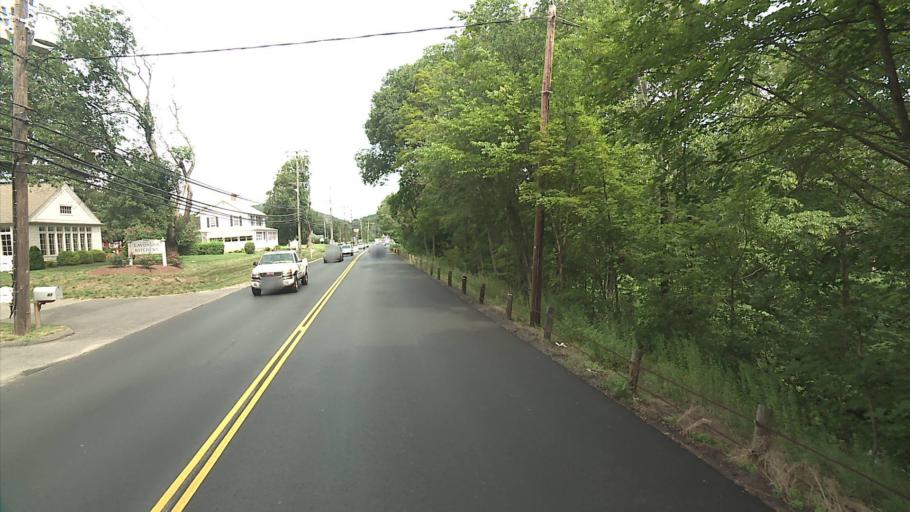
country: US
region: Connecticut
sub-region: New Haven County
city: Seymour
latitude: 41.4030
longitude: -73.0912
